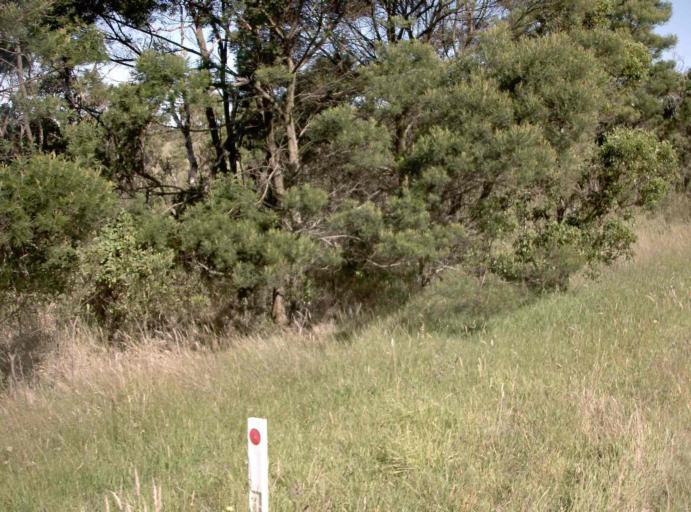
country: AU
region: Victoria
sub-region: Latrobe
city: Traralgon
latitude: -38.6228
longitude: 146.6731
